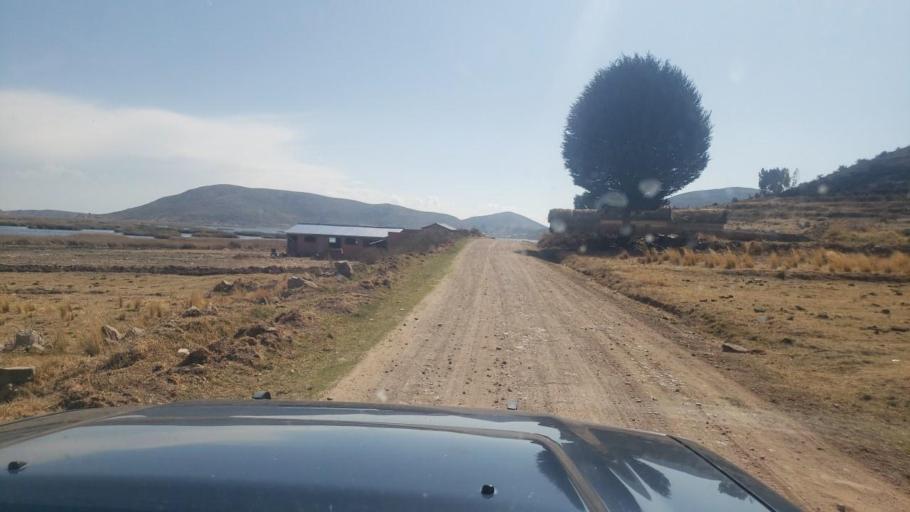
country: BO
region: La Paz
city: Huatajata
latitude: -16.3383
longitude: -68.6858
